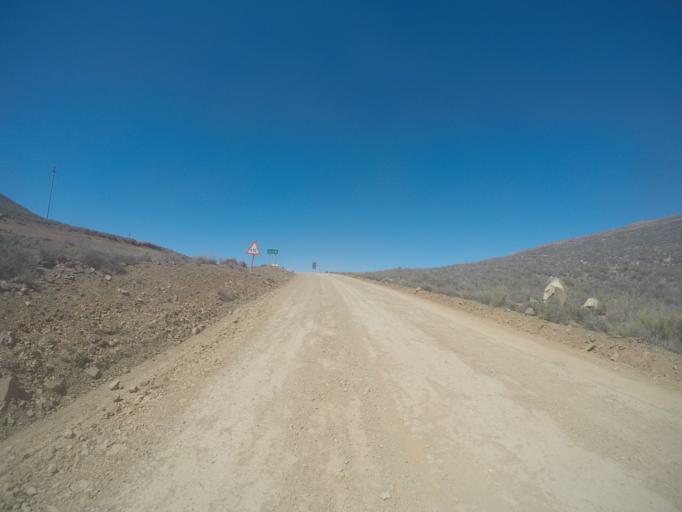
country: ZA
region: Western Cape
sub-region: West Coast District Municipality
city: Clanwilliam
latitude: -32.6096
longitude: 19.3673
